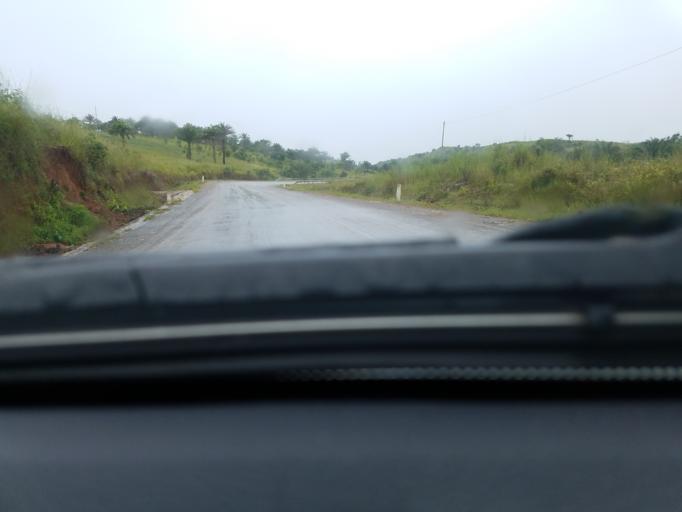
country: TZ
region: Kigoma
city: Mwandiga
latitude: -4.6709
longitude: 29.7248
